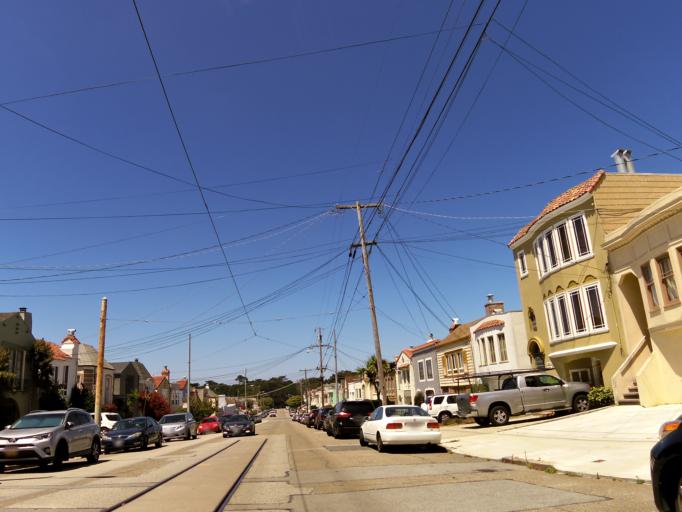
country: US
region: California
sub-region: San Mateo County
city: Daly City
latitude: 37.7617
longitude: -122.4888
